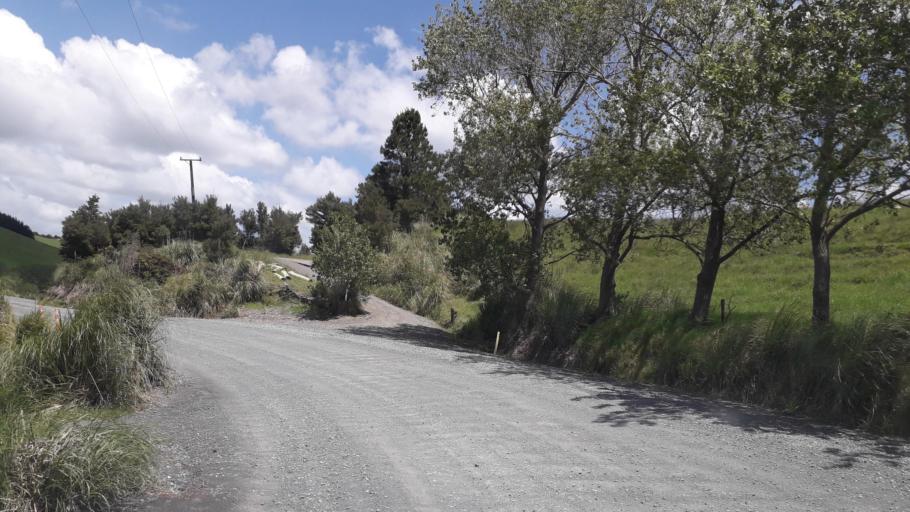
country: NZ
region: Northland
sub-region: Far North District
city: Taipa
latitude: -35.0052
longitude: 173.4313
